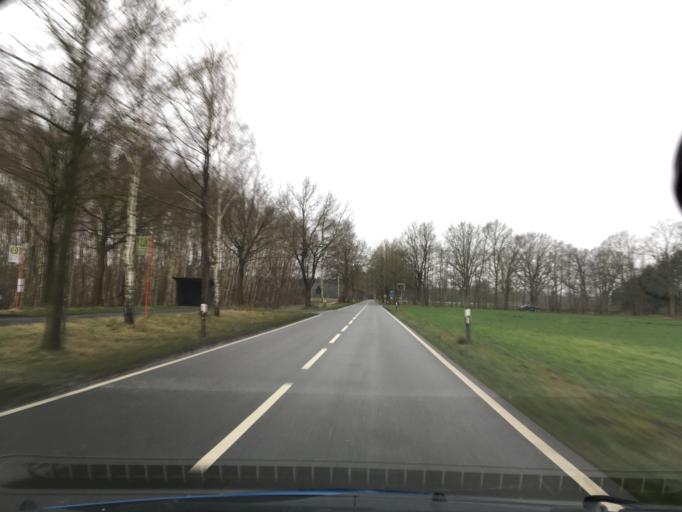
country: DE
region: Lower Saxony
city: Neetze
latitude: 53.3014
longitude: 10.6578
